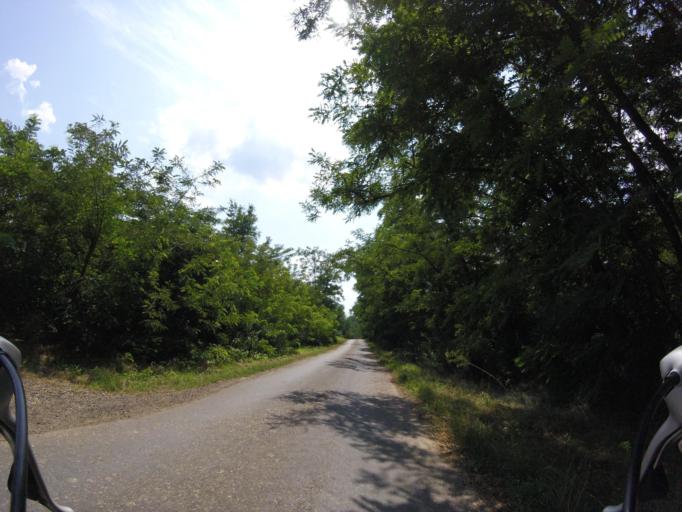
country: SK
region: Nitriansky
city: Sahy
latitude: 48.0361
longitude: 18.8381
